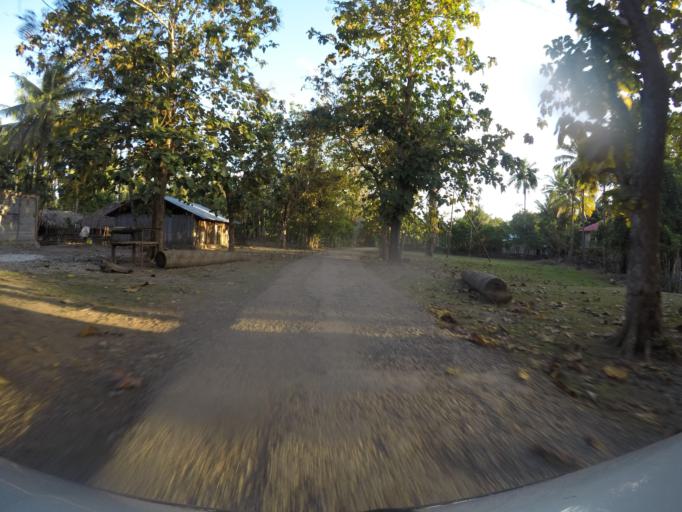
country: TL
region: Baucau
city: Venilale
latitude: -8.7392
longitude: 126.7147
